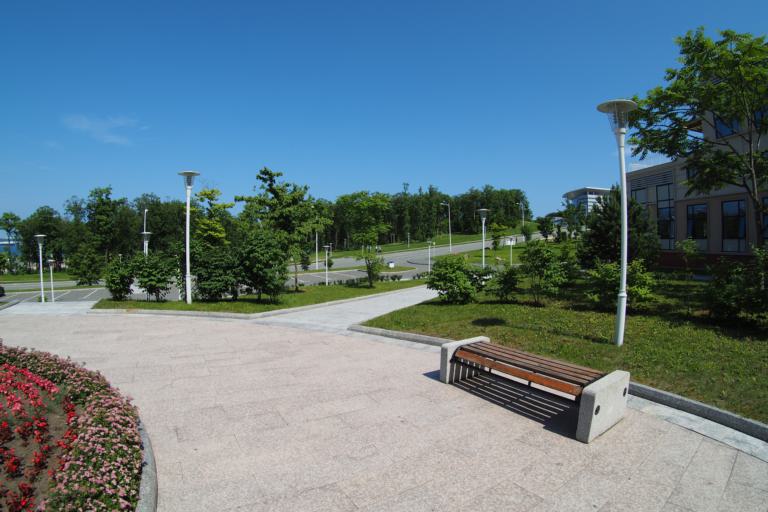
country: RU
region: Primorskiy
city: Russkiy
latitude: 43.0278
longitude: 131.8891
